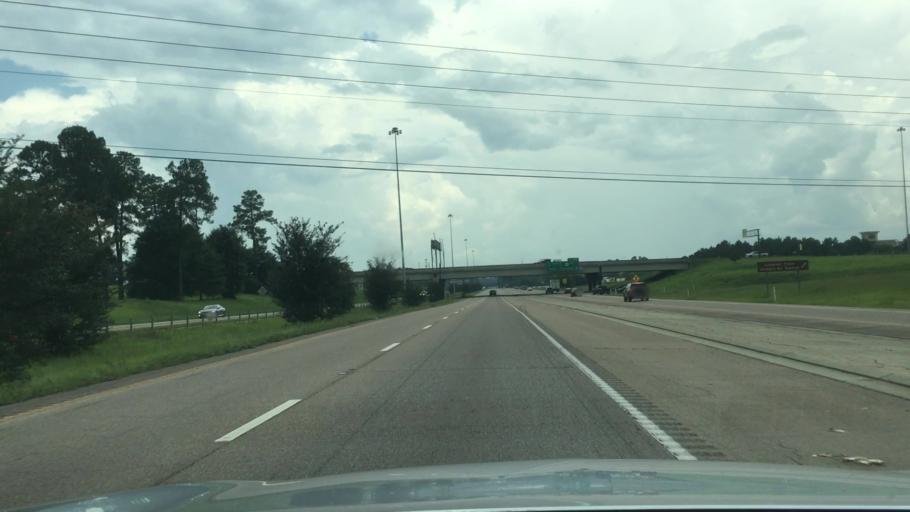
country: US
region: Mississippi
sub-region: Lamar County
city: West Hattiesburg
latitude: 31.3228
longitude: -89.3523
